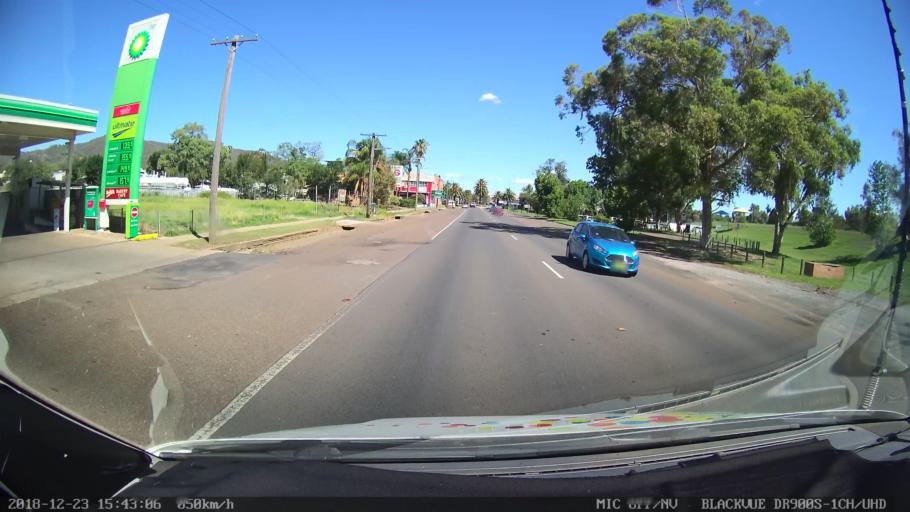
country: AU
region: New South Wales
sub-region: Tamworth Municipality
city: Tamworth
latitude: -31.0854
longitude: 150.9250
